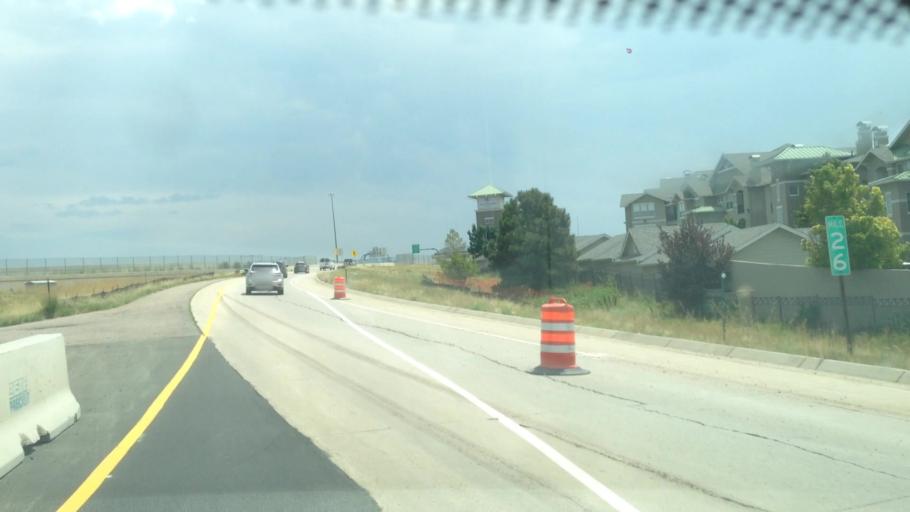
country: US
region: Colorado
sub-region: Adams County
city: Lone Tree
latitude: 39.5543
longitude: -104.8727
